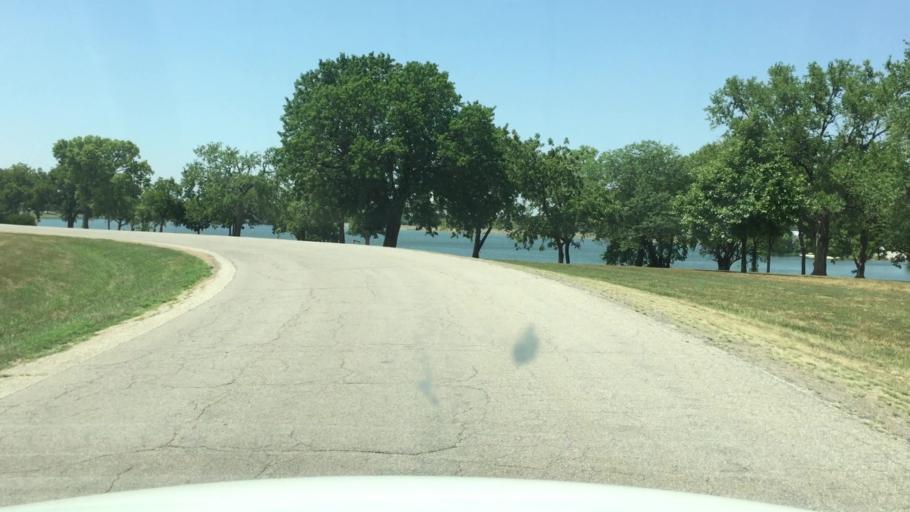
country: US
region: Kansas
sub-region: Shawnee County
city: Topeka
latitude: 39.0103
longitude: -95.6221
